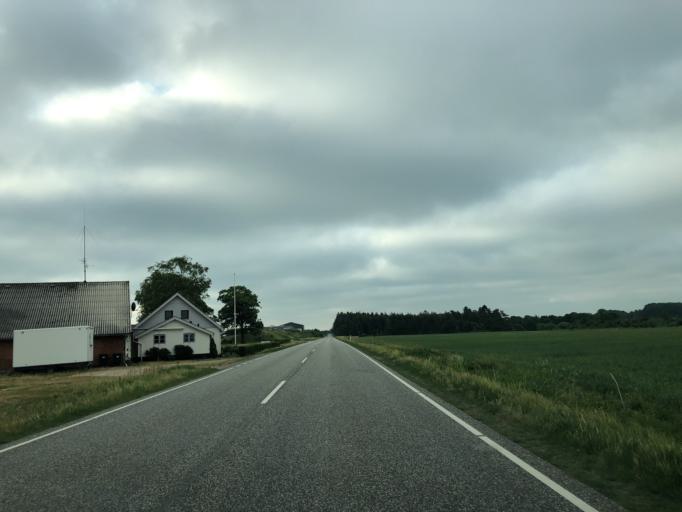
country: DK
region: Central Jutland
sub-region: Ikast-Brande Kommune
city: Brande
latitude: 55.9086
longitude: 9.1883
